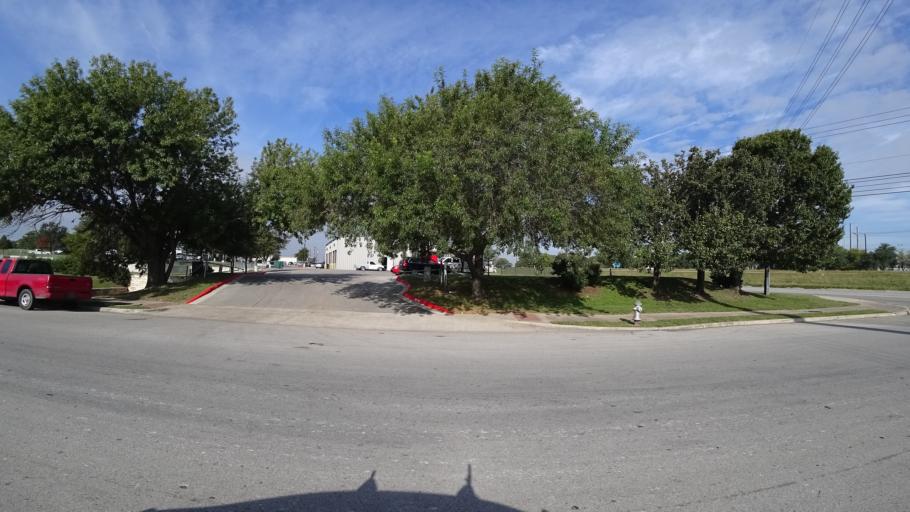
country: US
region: Texas
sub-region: Travis County
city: Austin
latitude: 30.2129
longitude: -97.7235
